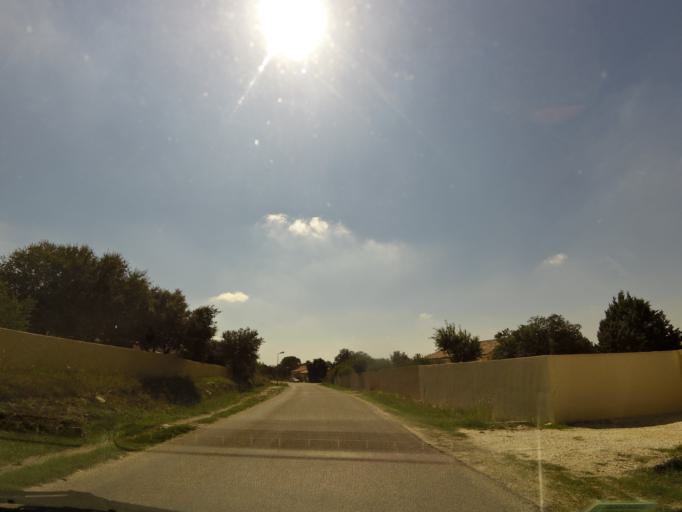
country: FR
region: Languedoc-Roussillon
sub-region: Departement du Gard
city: Villevieille
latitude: 43.7928
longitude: 4.1186
